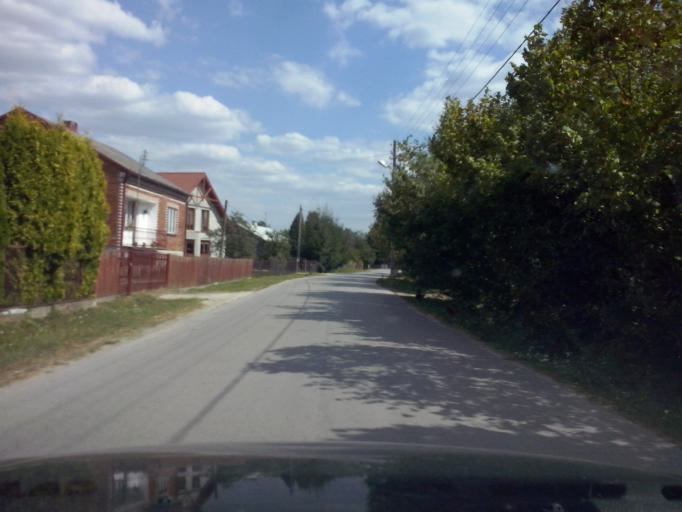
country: PL
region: Swietokrzyskie
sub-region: Powiat staszowski
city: Staszow
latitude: 50.5447
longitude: 21.1195
